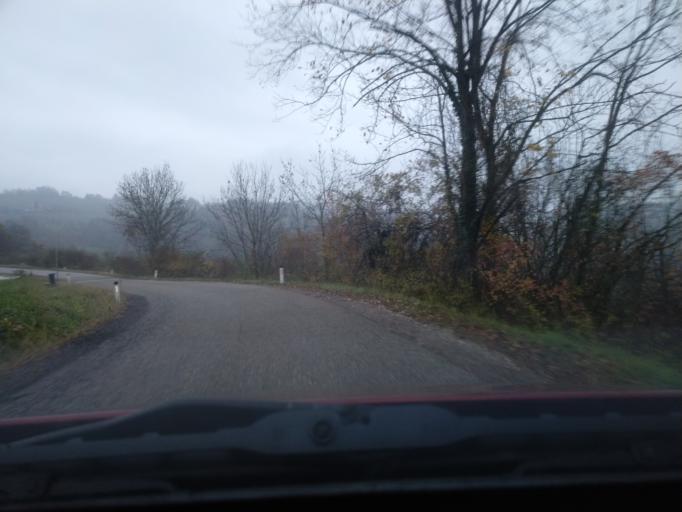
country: SI
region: Kungota
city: Zgornja Kungota
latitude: 46.6769
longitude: 15.6091
